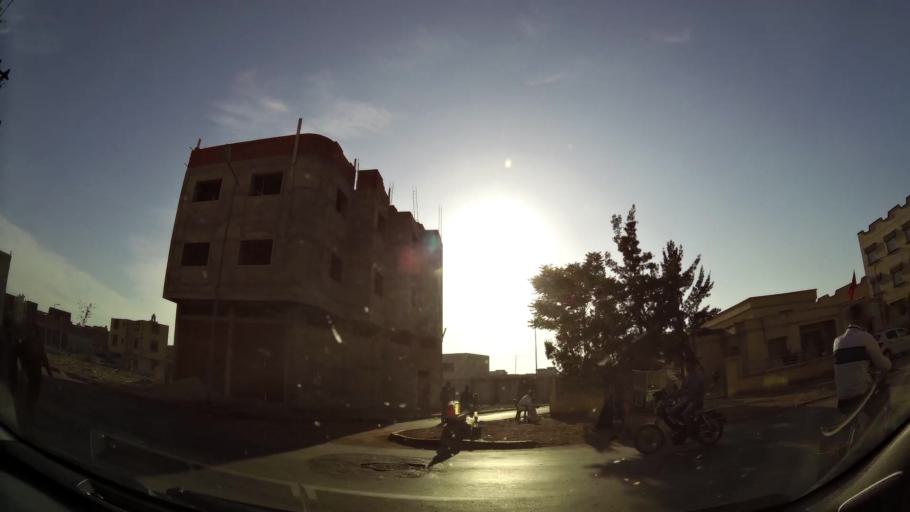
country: MA
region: Oriental
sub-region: Oujda-Angad
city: Oujda
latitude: 34.7093
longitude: -1.8965
